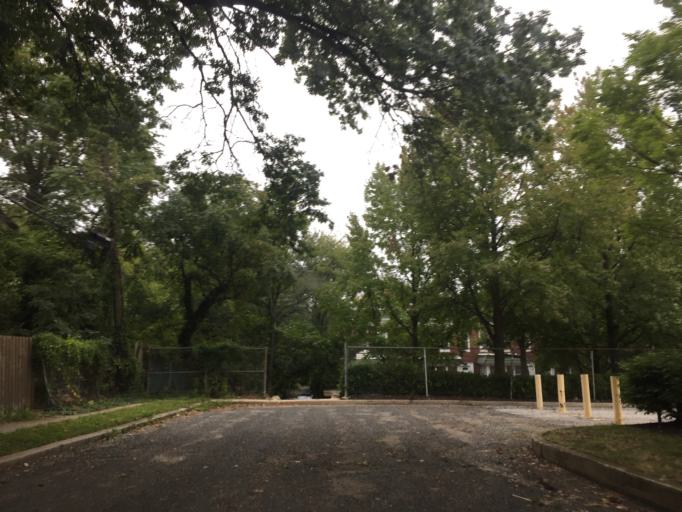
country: US
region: Maryland
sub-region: City of Baltimore
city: Baltimore
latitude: 39.3268
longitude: -76.6034
